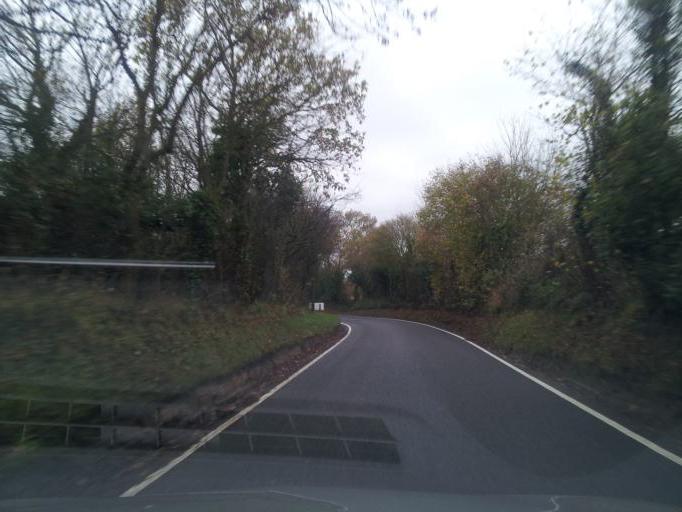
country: GB
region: England
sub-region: Essex
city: Eight Ash Green
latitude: 51.9187
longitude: 0.7975
